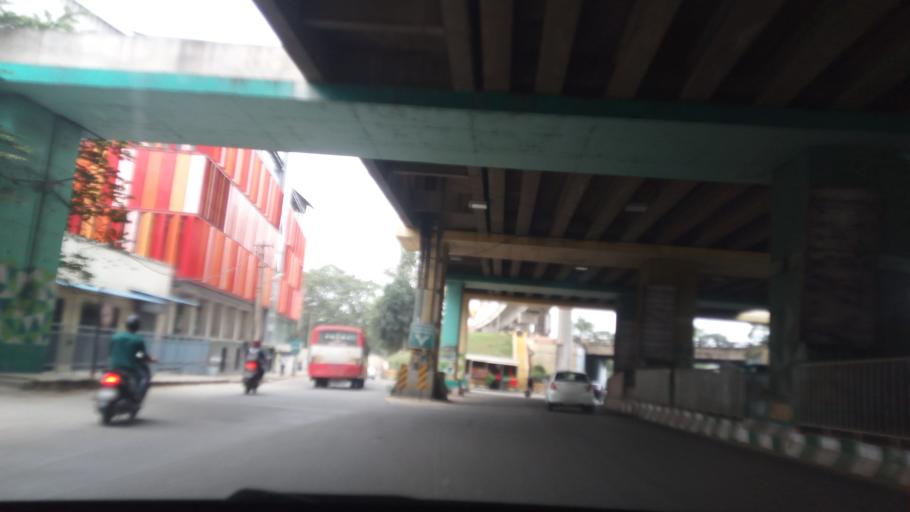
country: IN
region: Karnataka
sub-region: Bangalore Urban
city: Bangalore
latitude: 13.0148
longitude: 77.5539
